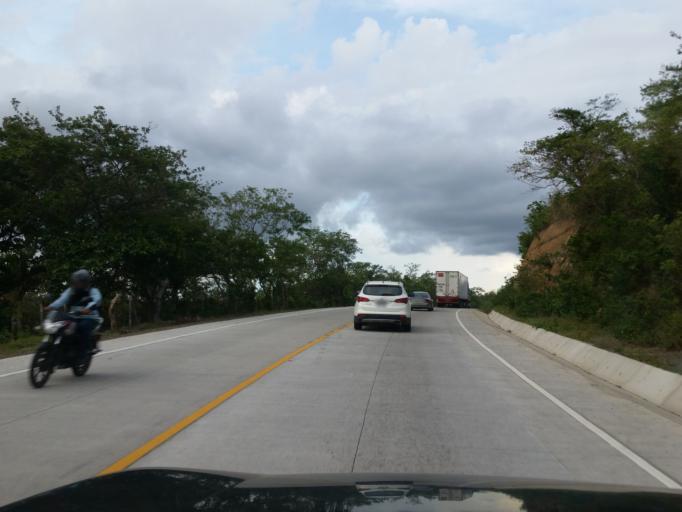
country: NI
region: Managua
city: Ciudad Sandino
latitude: 12.0796
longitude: -86.4220
